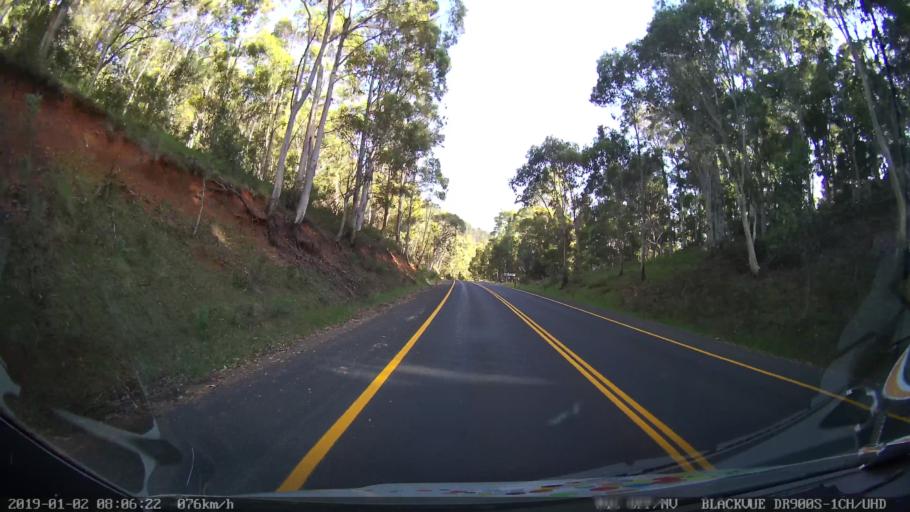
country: AU
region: New South Wales
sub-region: Tumut Shire
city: Tumut
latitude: -35.6409
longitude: 148.3871
